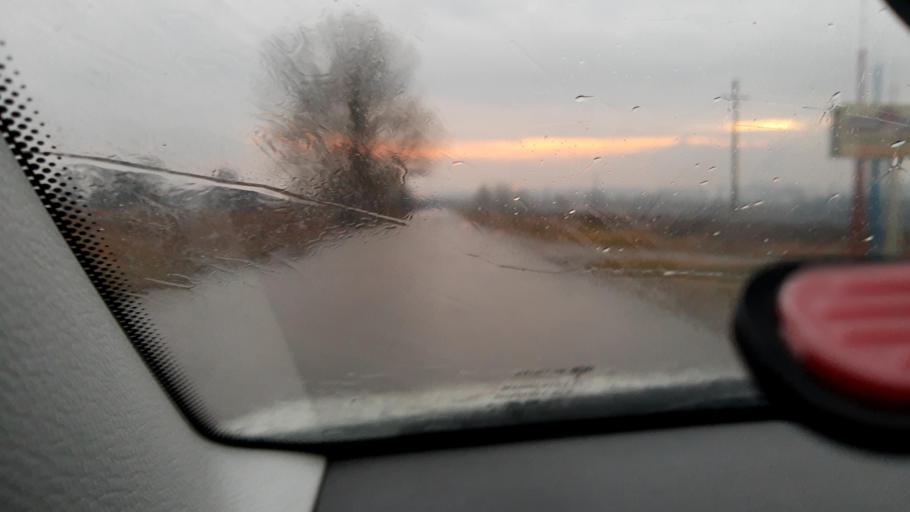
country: RU
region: Bashkortostan
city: Blagoveshchensk
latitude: 54.8916
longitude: 56.1478
